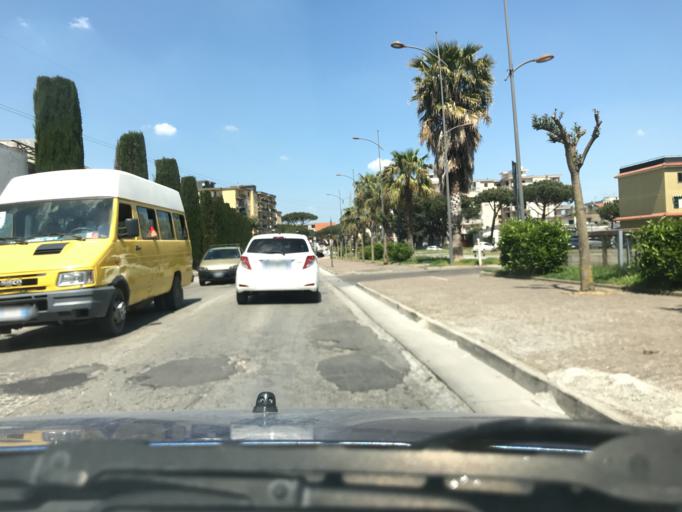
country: IT
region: Campania
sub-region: Provincia di Napoli
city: Villaricca
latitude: 40.9185
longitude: 14.1822
